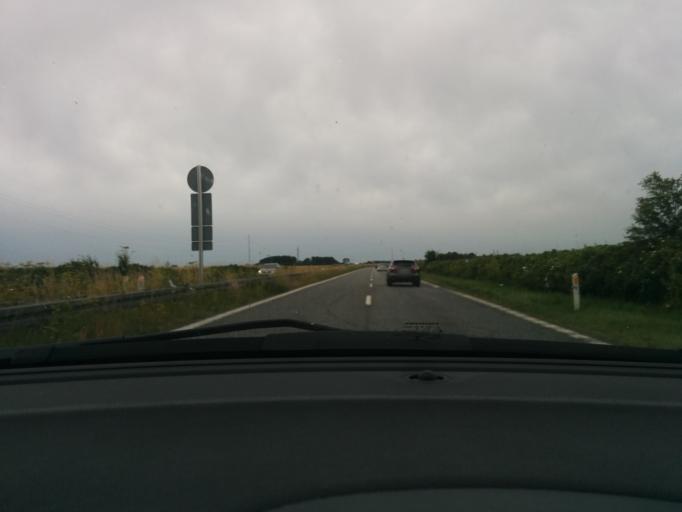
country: DK
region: Zealand
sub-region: Lolland Kommune
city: Rodby
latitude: 54.6857
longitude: 11.4023
